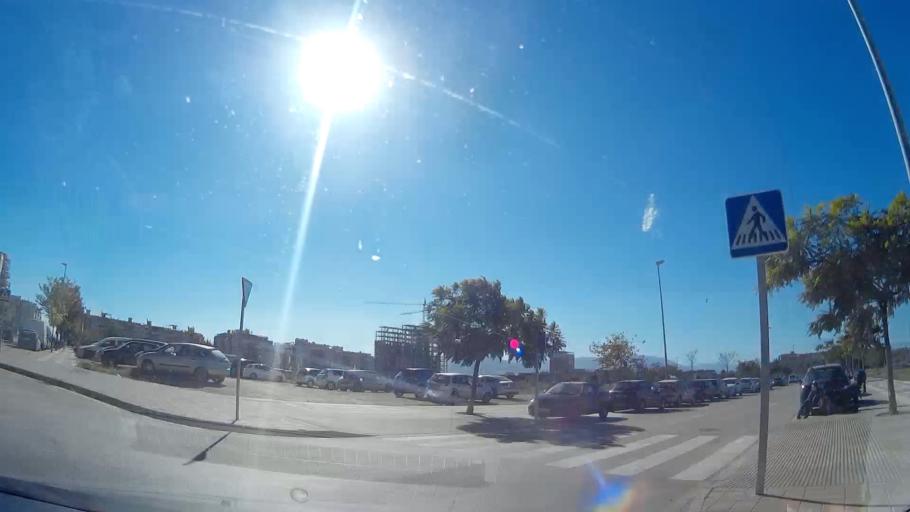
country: ES
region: Andalusia
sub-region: Provincia de Malaga
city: Malaga
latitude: 36.7193
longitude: -4.4645
